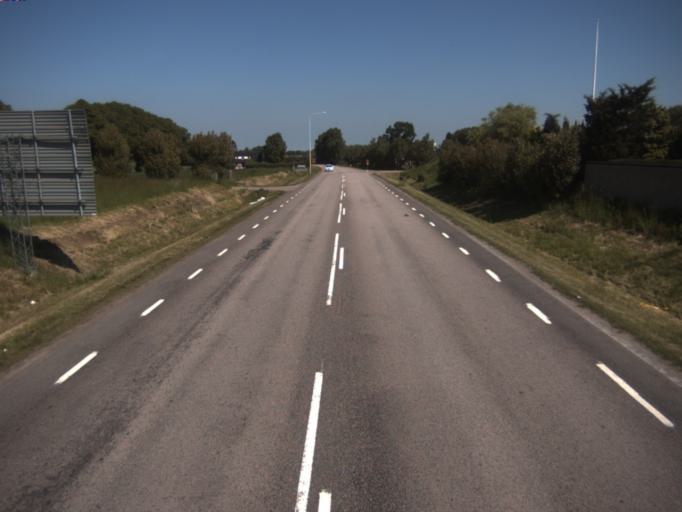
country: SE
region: Skane
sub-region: Helsingborg
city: Barslov
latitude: 56.0182
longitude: 12.7945
